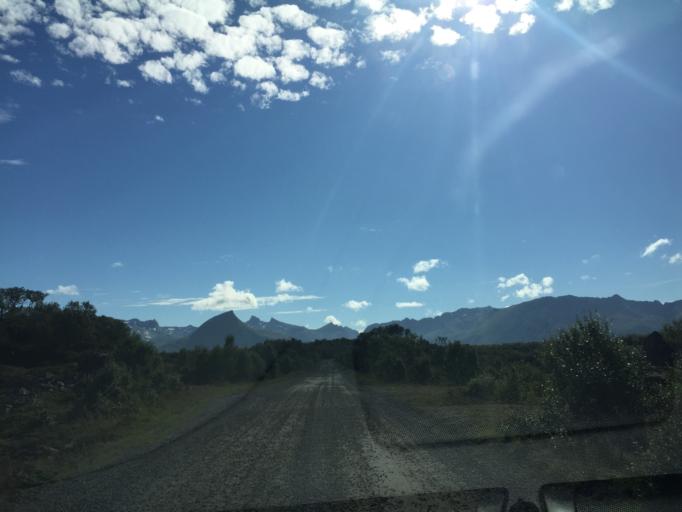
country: NO
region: Nordland
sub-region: Vagan
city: Kabelvag
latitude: 68.3640
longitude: 14.4561
